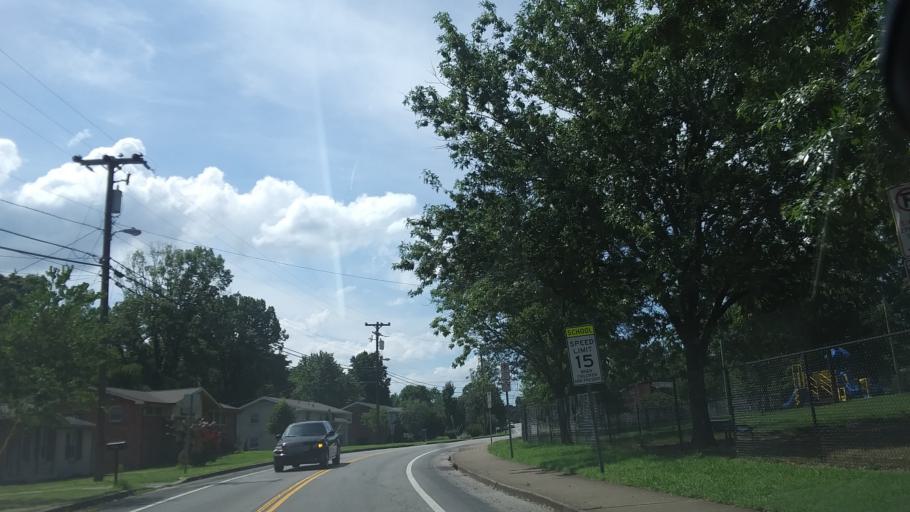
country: US
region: Tennessee
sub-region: Rutherford County
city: La Vergne
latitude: 36.0781
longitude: -86.6312
